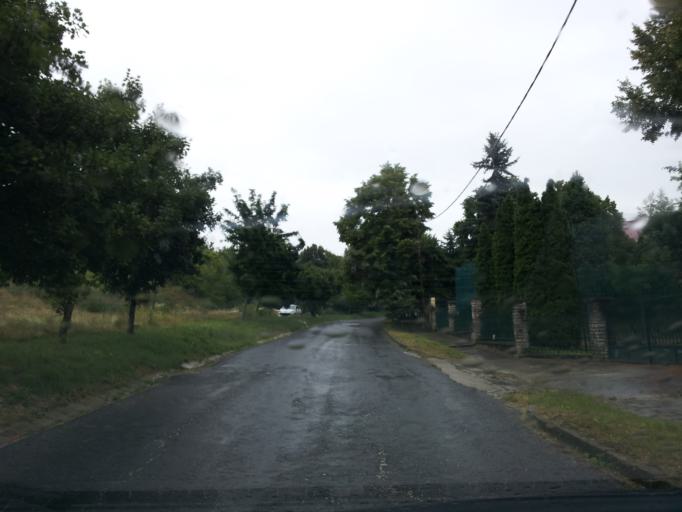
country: HU
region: Veszprem
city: Balatonkenese
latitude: 47.0158
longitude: 18.1633
